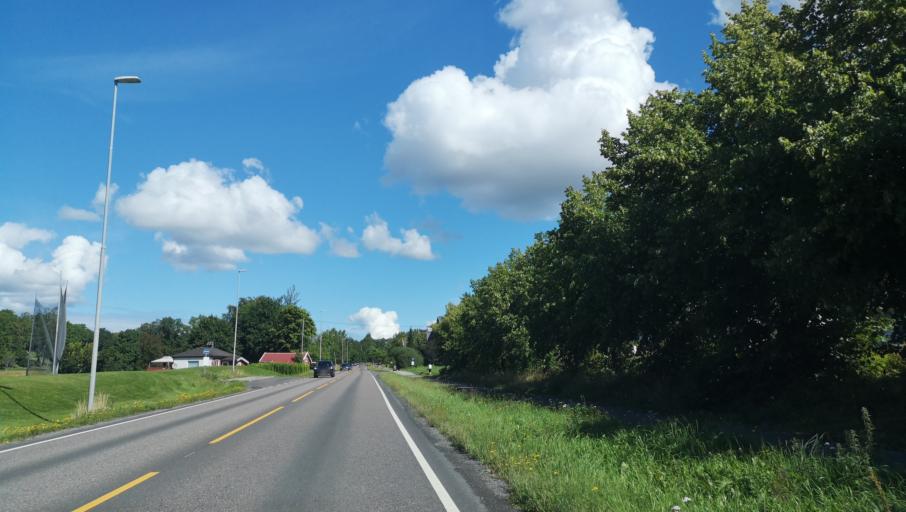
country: NO
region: Akershus
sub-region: Frogn
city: Drobak
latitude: 59.6692
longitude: 10.6477
